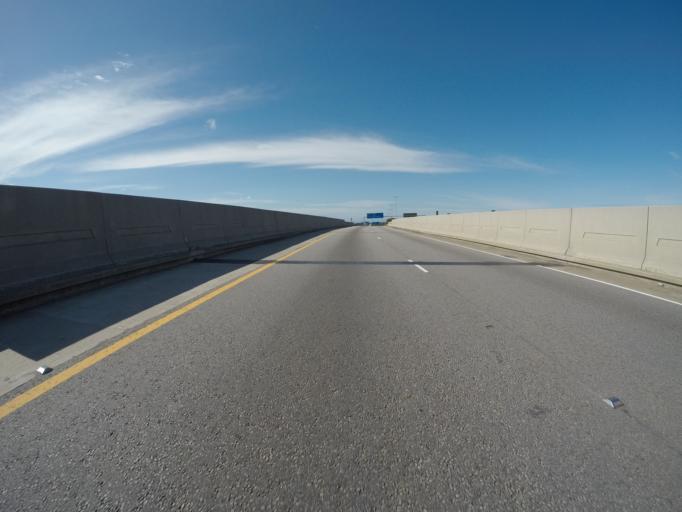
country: ZA
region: Eastern Cape
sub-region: Nelson Mandela Bay Metropolitan Municipality
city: Port Elizabeth
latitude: -33.9138
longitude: 25.6050
